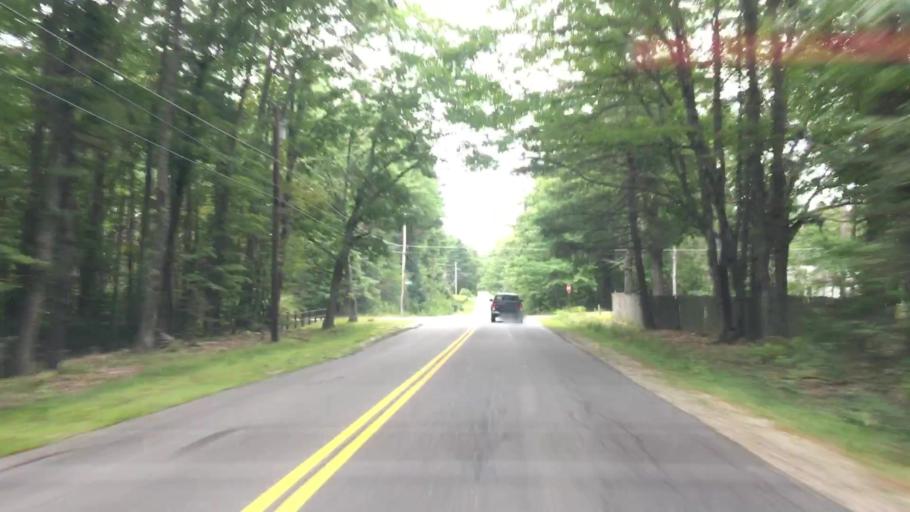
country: US
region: Maine
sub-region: Cumberland County
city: Freeport
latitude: 43.8768
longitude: -70.1526
